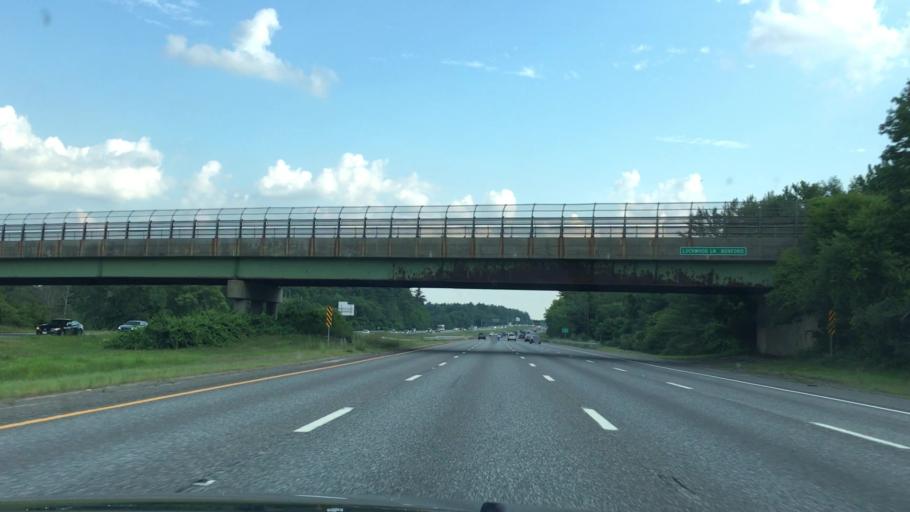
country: US
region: Massachusetts
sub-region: Essex County
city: Boxford
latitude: 42.6429
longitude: -70.9772
